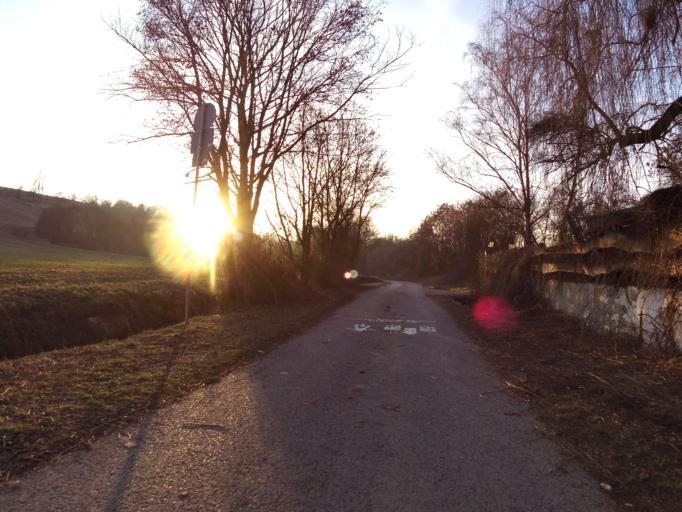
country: DE
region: Bavaria
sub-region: Regierungsbezirk Unterfranken
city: Estenfeld
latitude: 49.8212
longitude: 10.0166
